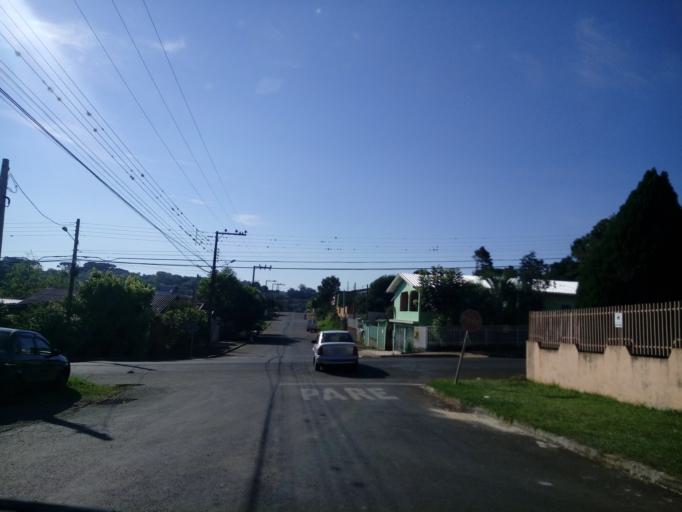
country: BR
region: Santa Catarina
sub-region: Chapeco
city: Chapeco
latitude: -27.0982
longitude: -52.6690
